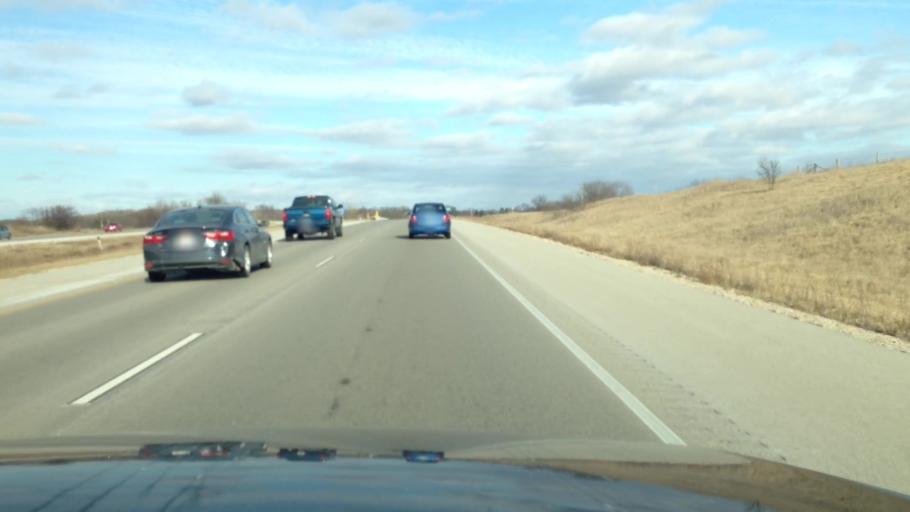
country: US
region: Wisconsin
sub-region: Waukesha County
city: Big Bend
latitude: 42.8964
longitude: -88.2622
